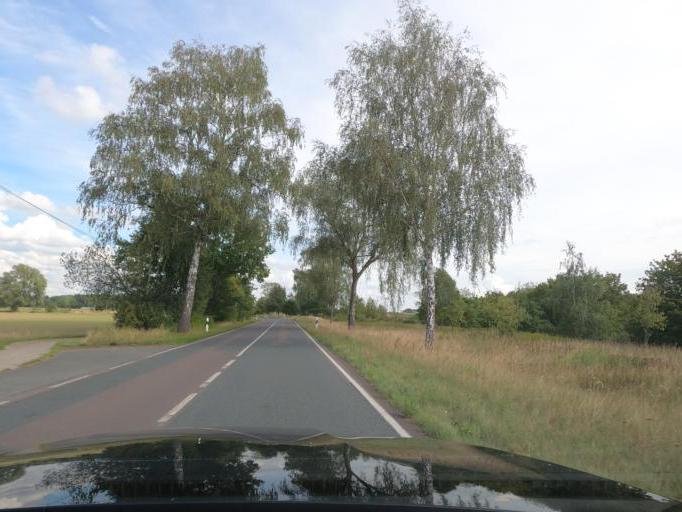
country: DE
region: Lower Saxony
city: Burgdorf
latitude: 52.4555
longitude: 9.9490
